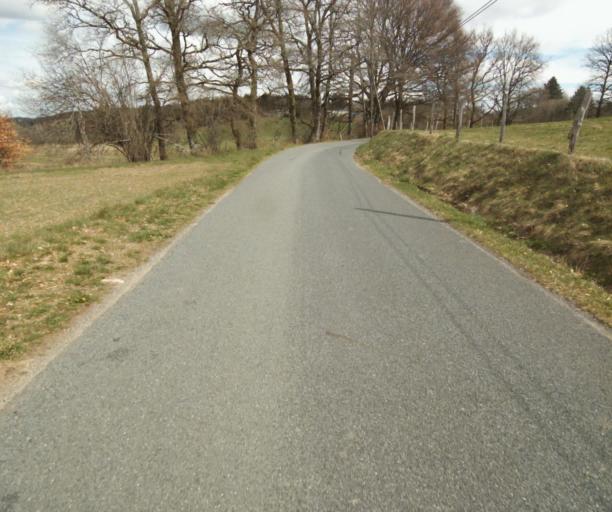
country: FR
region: Limousin
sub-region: Departement de la Correze
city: Correze
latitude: 45.3851
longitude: 1.9579
